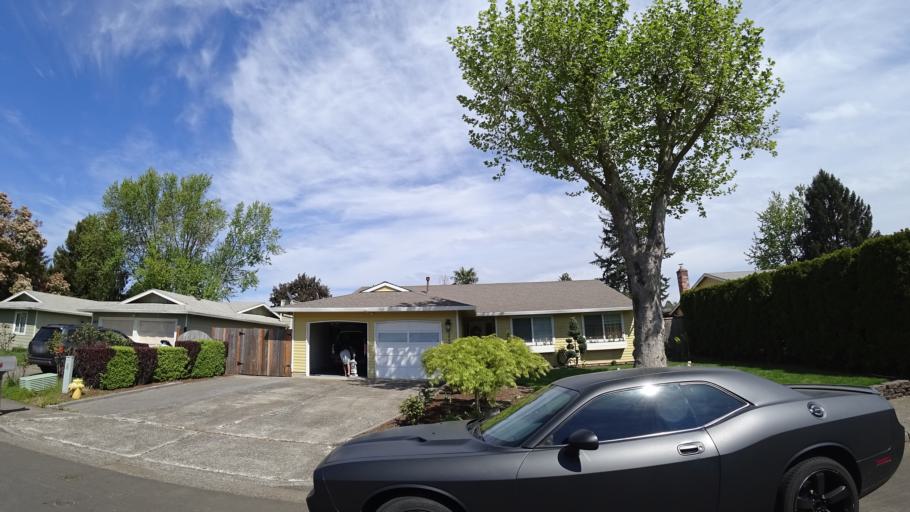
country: US
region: Oregon
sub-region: Washington County
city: Aloha
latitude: 45.4909
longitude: -122.8879
